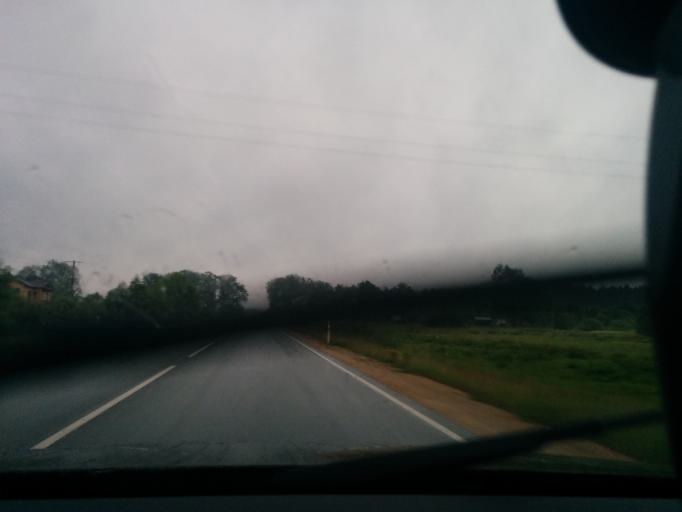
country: LV
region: Salaspils
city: Salaspils
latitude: 56.8998
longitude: 24.4147
